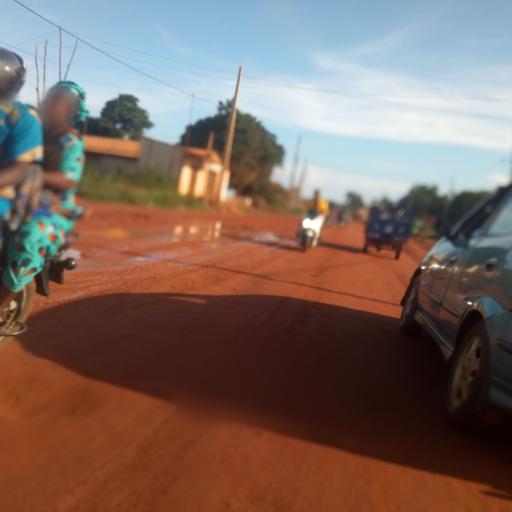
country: BJ
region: Atlantique
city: Hevie
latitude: 6.4229
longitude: 2.2598
